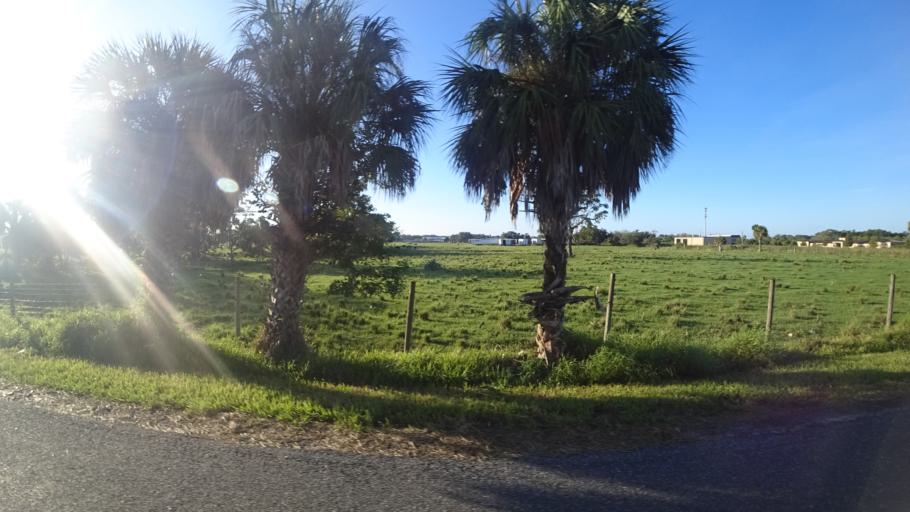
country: US
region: Florida
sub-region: Manatee County
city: Ellenton
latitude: 27.5327
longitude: -82.5389
